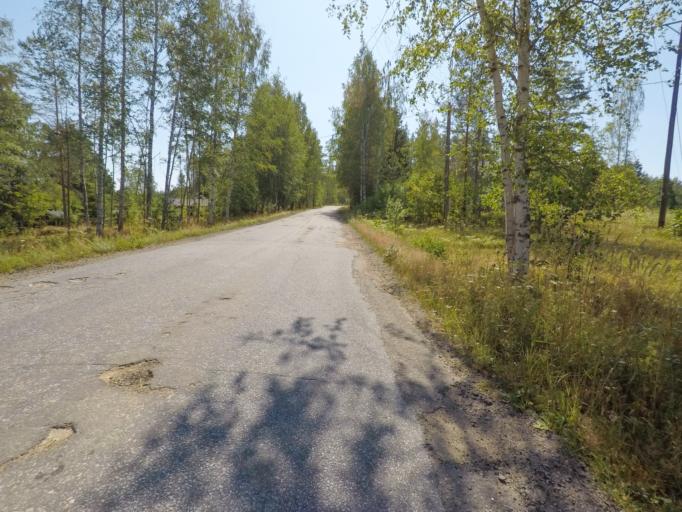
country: FI
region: Southern Savonia
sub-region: Mikkeli
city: Puumala
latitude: 61.4209
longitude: 28.0932
